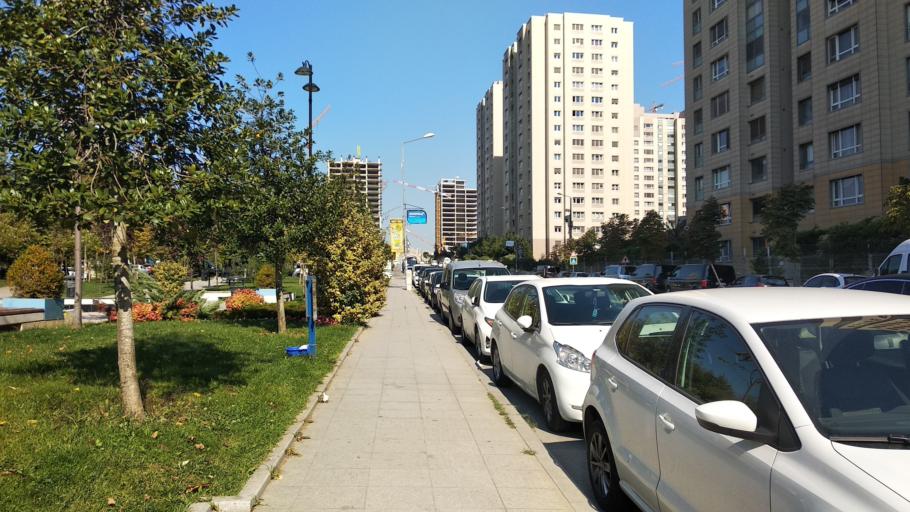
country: TR
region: Istanbul
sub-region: Atasehir
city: Atasehir
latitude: 40.9986
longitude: 29.1031
